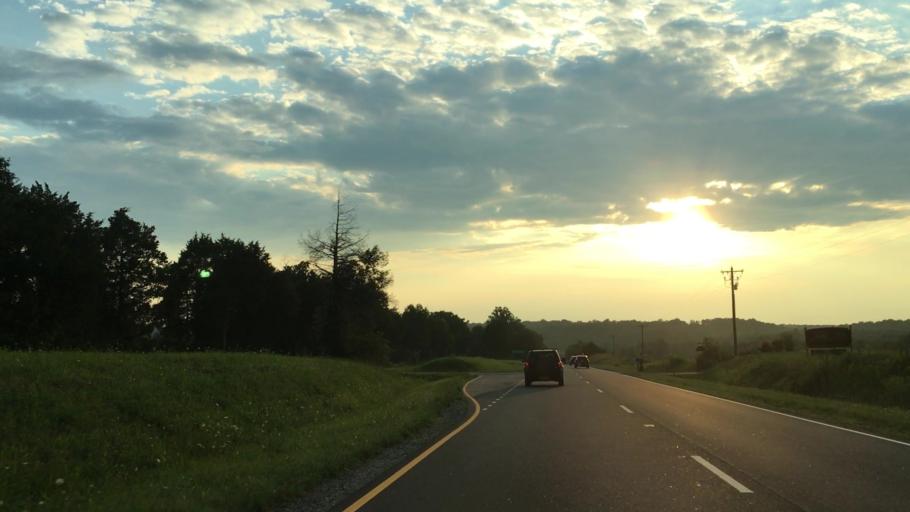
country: US
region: Virginia
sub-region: Spotsylvania County
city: Spotsylvania
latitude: 38.3244
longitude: -77.7187
